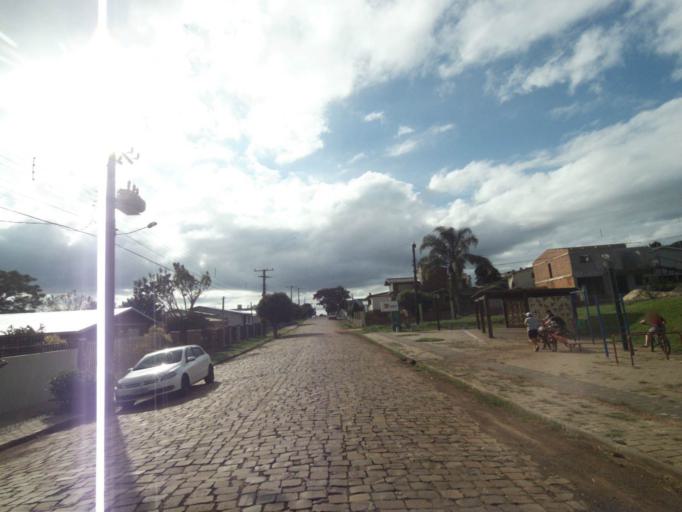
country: BR
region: Rio Grande do Sul
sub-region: Lagoa Vermelha
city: Lagoa Vermelha
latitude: -28.2051
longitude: -51.5162
